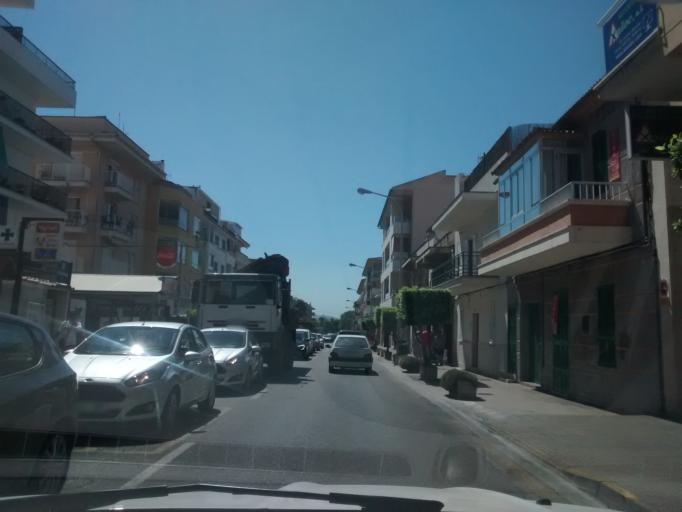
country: ES
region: Balearic Islands
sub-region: Illes Balears
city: Alcudia
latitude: 39.8515
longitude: 3.1256
